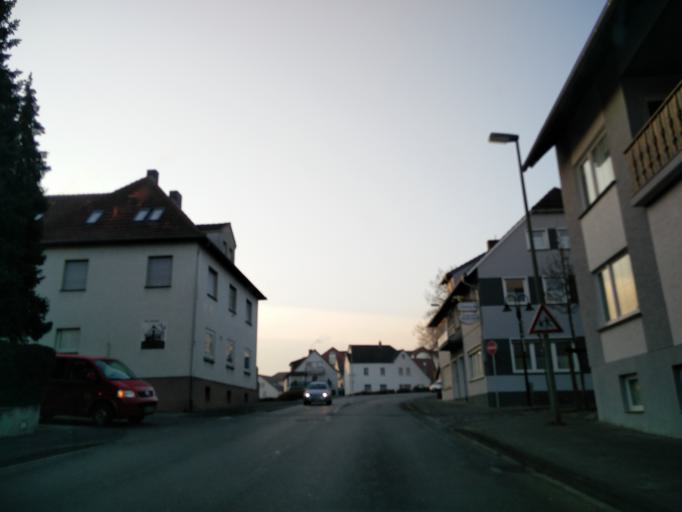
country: DE
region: North Rhine-Westphalia
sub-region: Regierungsbezirk Detmold
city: Buren
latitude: 51.5515
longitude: 8.5601
